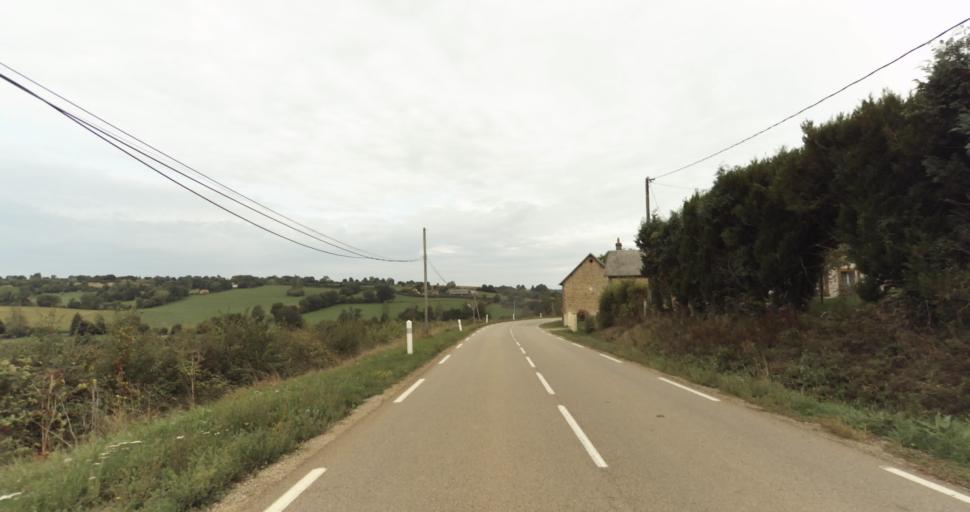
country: FR
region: Lower Normandy
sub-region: Departement de l'Orne
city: Gace
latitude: 48.7606
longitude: 0.3389
